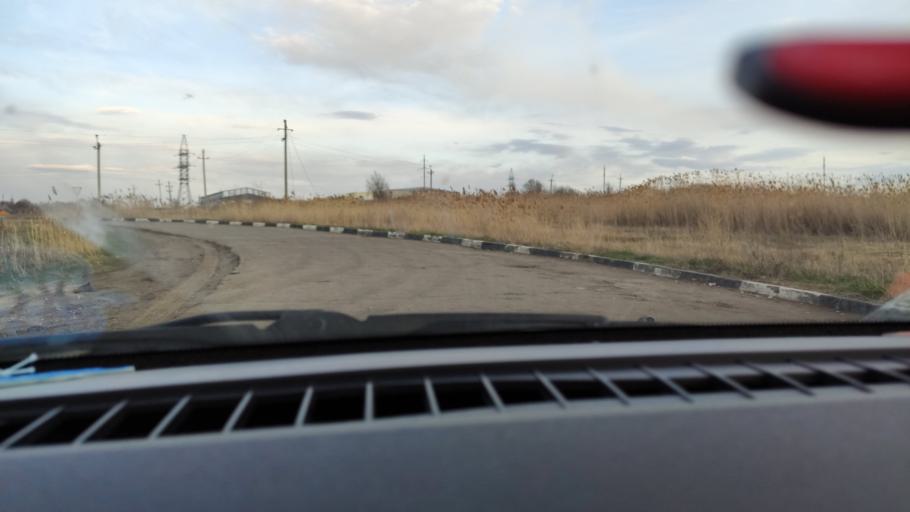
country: RU
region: Saratov
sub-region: Saratovskiy Rayon
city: Saratov
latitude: 51.6181
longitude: 45.9480
